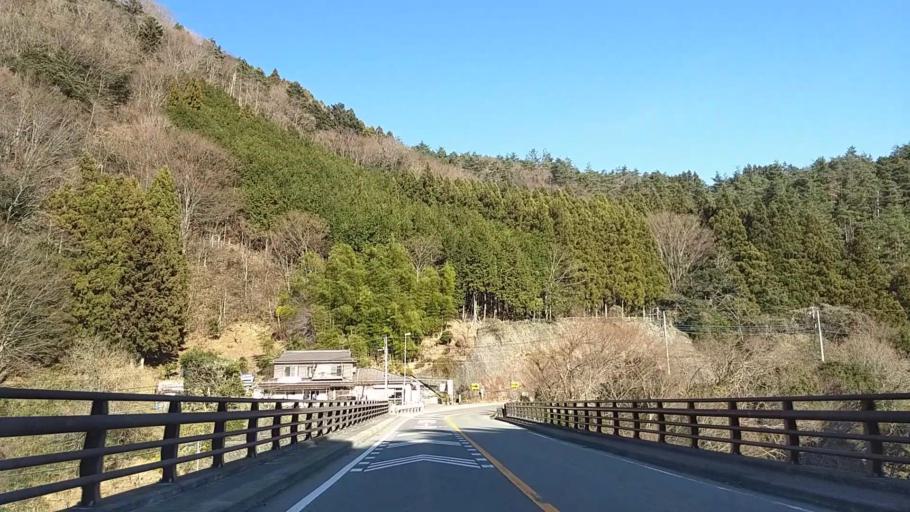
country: JP
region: Yamanashi
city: Uenohara
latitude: 35.5346
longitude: 139.0737
